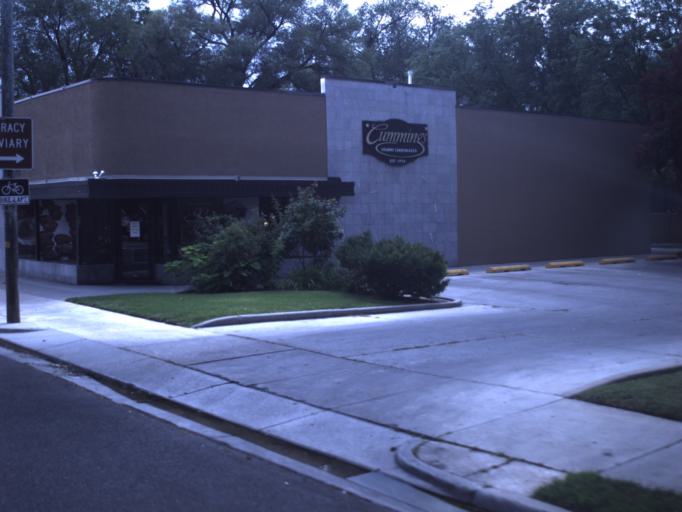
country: US
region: Utah
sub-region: Salt Lake County
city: Salt Lake City
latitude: 40.7503
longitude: -111.8712
